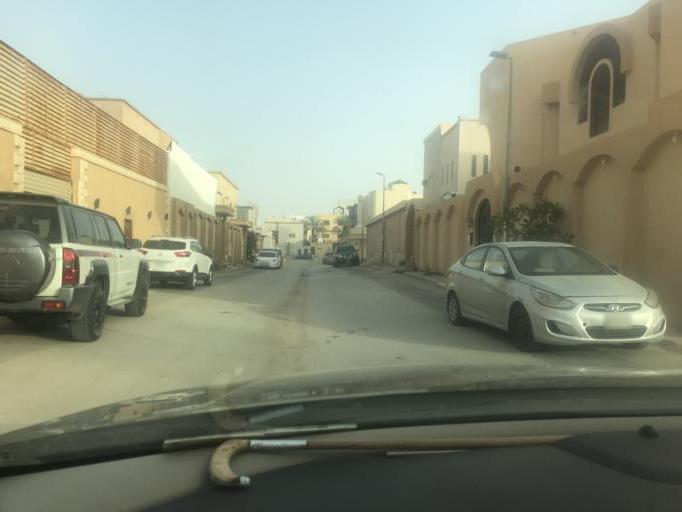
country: SA
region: Ar Riyad
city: Riyadh
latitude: 24.7439
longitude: 46.7712
